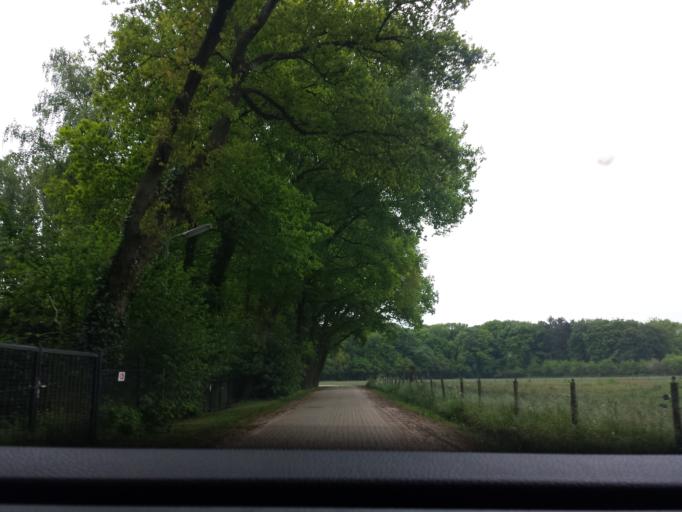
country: NL
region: Gelderland
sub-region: Gemeente Bronckhorst
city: Hengelo
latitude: 52.1005
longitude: 6.3169
